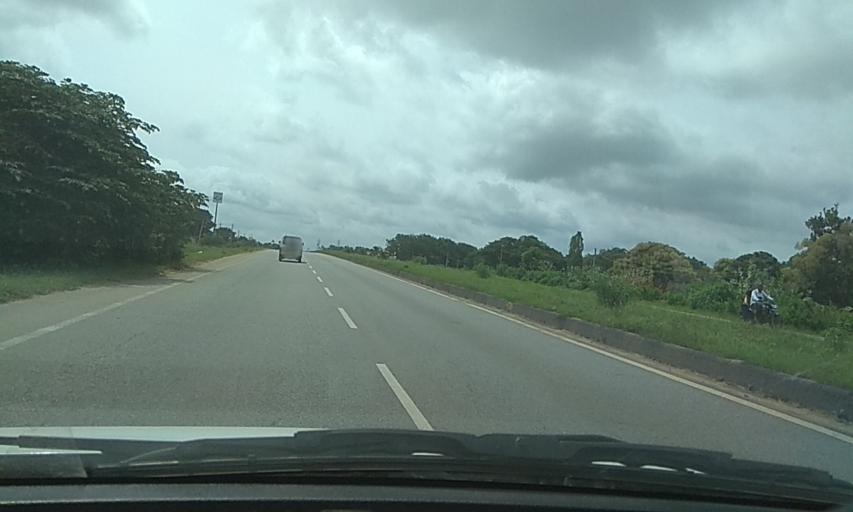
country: IN
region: Karnataka
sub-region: Davanagere
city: Mayakonda
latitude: 14.4205
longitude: 75.9793
